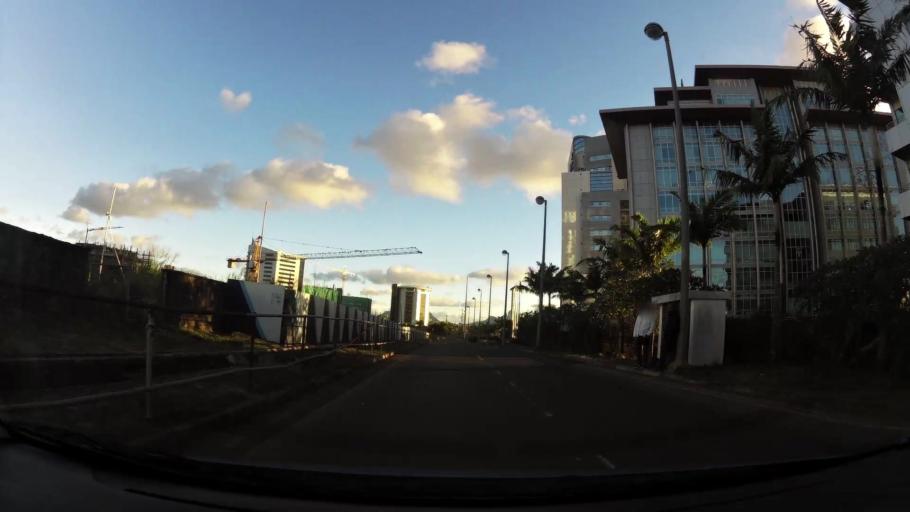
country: MU
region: Plaines Wilhems
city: Ebene
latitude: -20.2444
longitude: 57.4941
